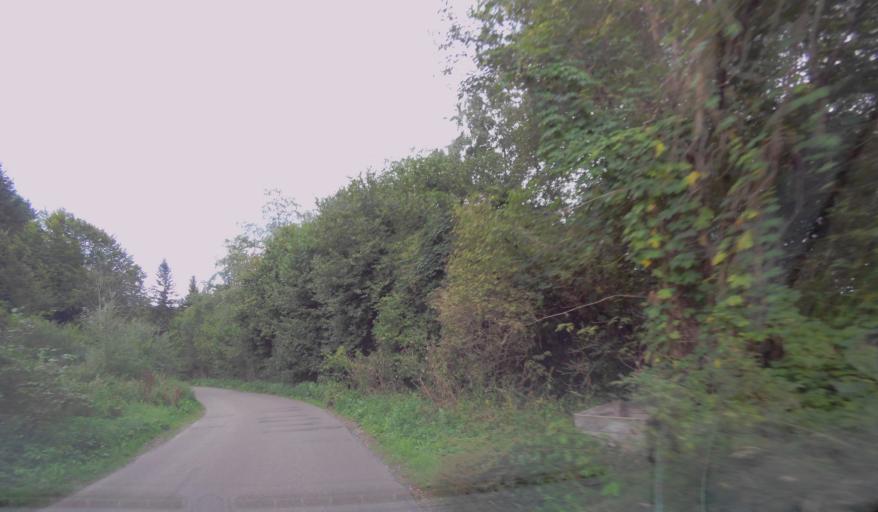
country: PL
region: Subcarpathian Voivodeship
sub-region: Powiat leski
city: Polanczyk
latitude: 49.3033
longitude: 22.5109
